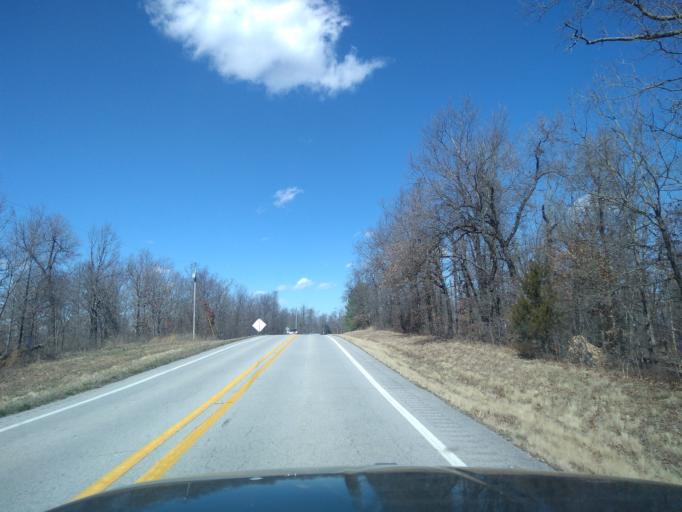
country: US
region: Arkansas
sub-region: Washington County
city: Farmington
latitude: 36.0895
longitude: -94.3308
